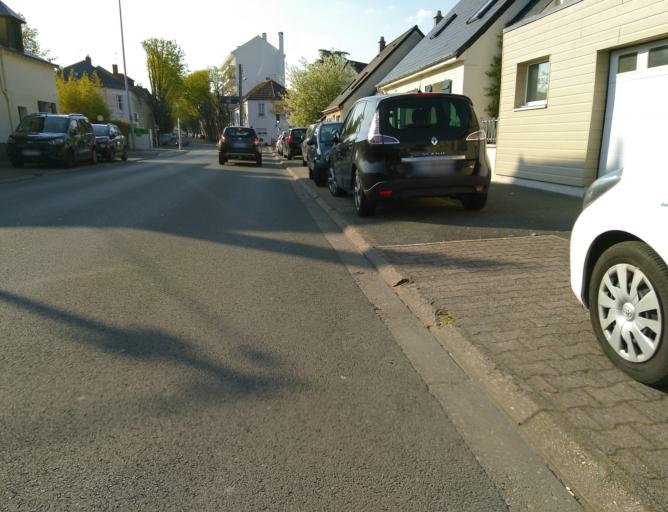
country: FR
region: Pays de la Loire
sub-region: Departement de Maine-et-Loire
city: Angers
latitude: 47.4545
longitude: -0.5476
